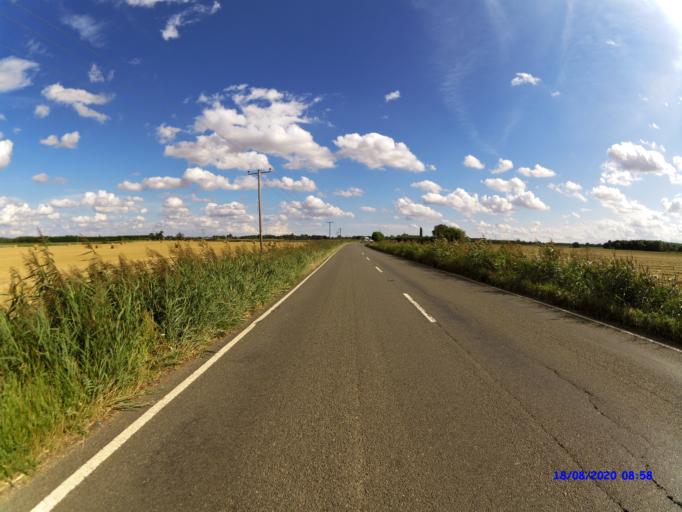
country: GB
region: England
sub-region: Cambridgeshire
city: Ramsey
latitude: 52.4775
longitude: -0.0990
